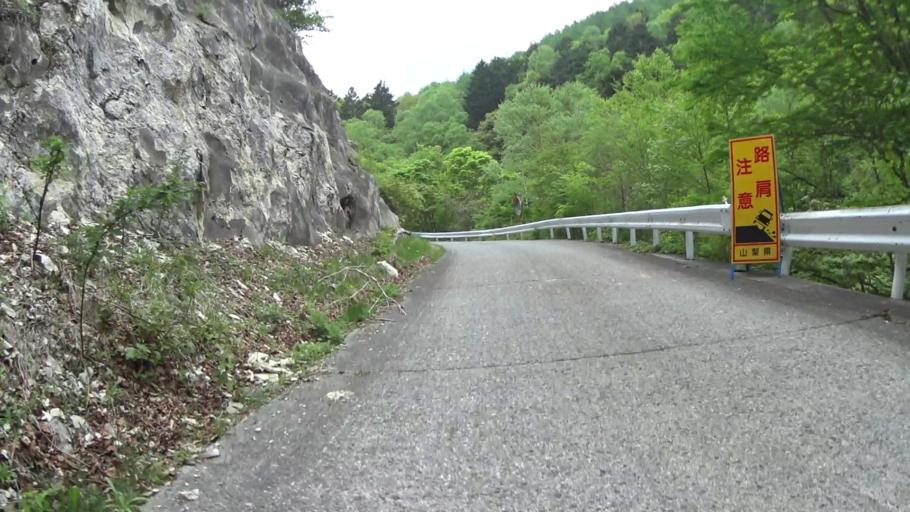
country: JP
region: Yamanashi
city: Kofu-shi
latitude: 35.8444
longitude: 138.5766
